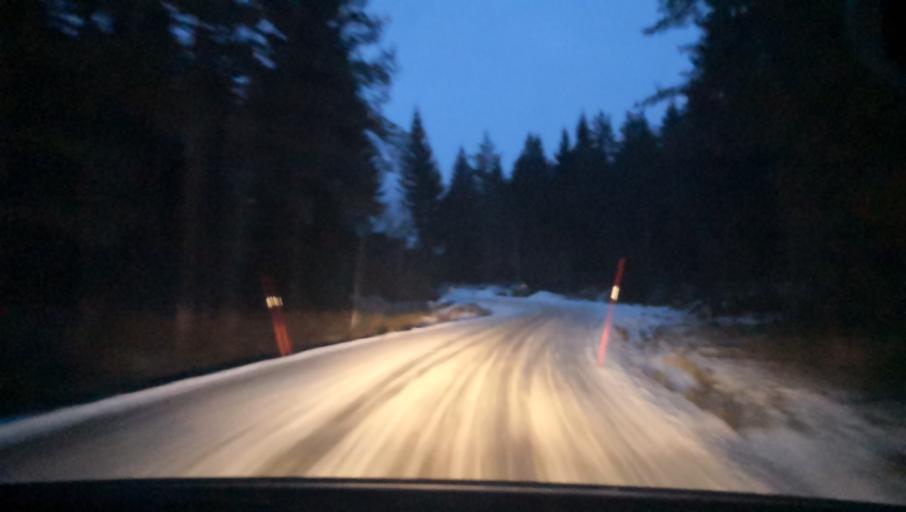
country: SE
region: Uppsala
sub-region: Heby Kommun
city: Tarnsjo
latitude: 60.2420
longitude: 16.7050
